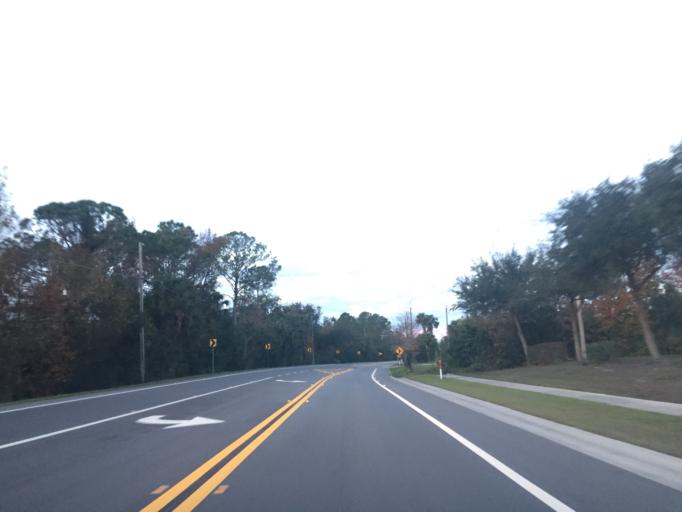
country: US
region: Florida
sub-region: Seminole County
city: Oviedo
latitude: 28.6854
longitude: -81.1641
